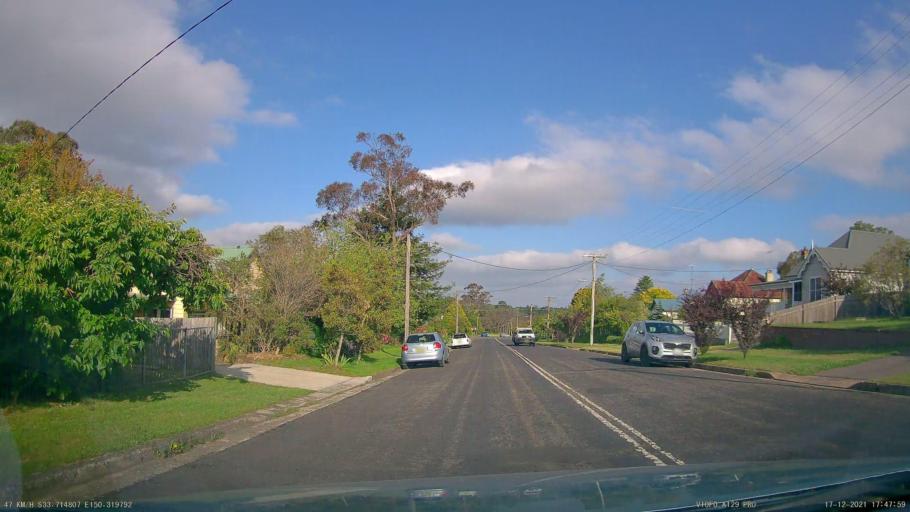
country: AU
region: New South Wales
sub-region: Blue Mountains Municipality
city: Leura
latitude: -33.7148
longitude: 150.3200
